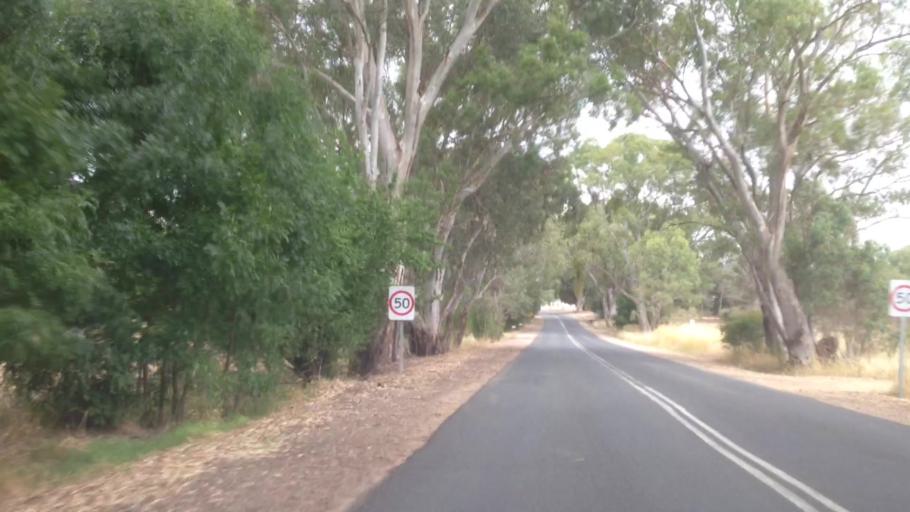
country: AU
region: South Australia
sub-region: Barossa
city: Williamstown
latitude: -34.6669
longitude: 138.8748
